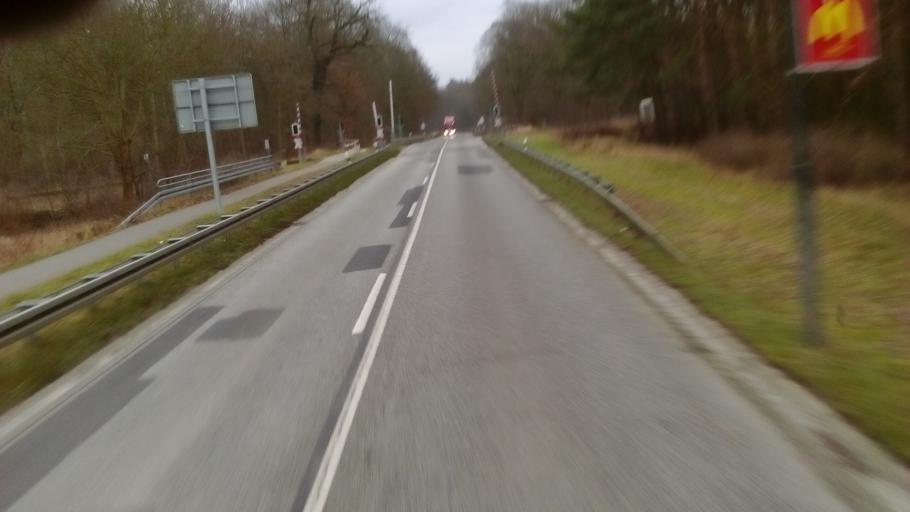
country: DE
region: Brandenburg
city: Brussow
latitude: 53.4531
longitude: 14.2290
